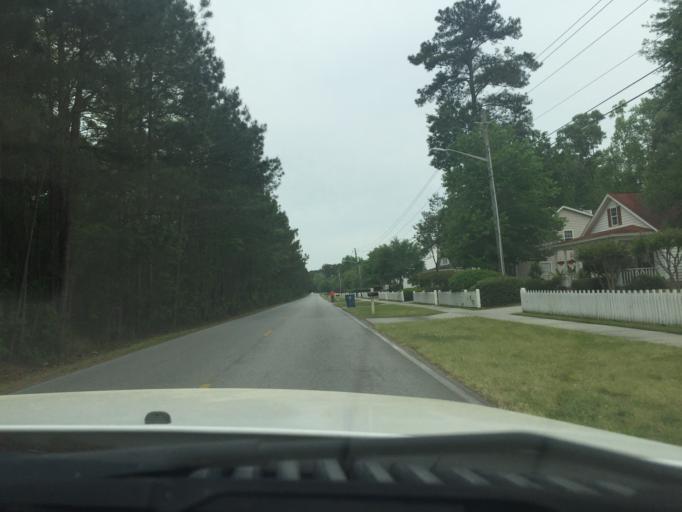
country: US
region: Georgia
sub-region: Chatham County
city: Georgetown
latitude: 31.9694
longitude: -81.2366
